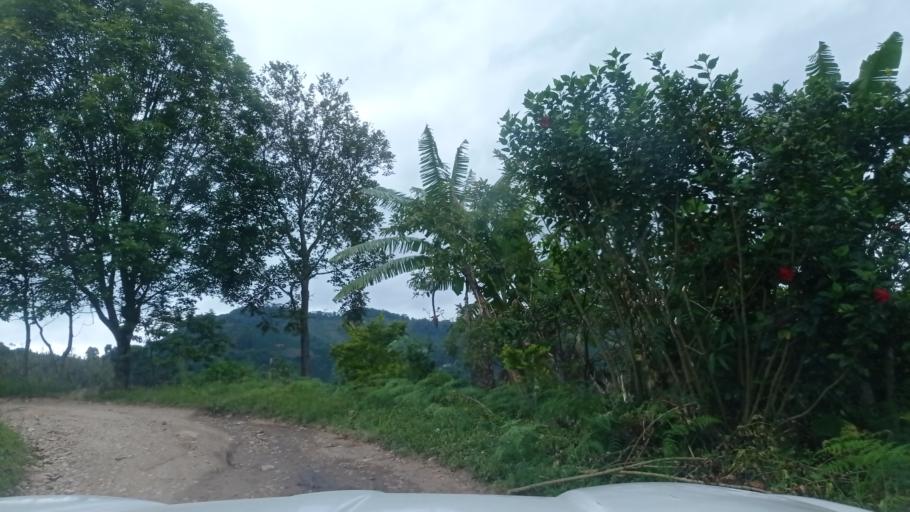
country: CO
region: Huila
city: Garzon
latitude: 2.0938
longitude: -75.6245
